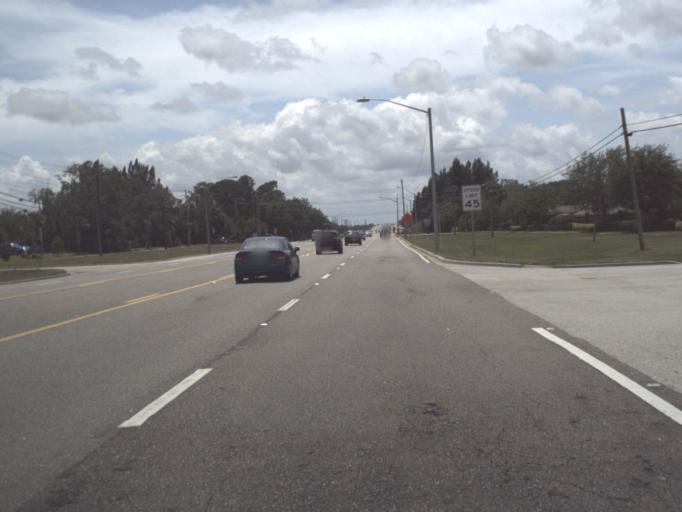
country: US
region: Florida
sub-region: Brevard County
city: Rockledge
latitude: 28.3047
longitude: -80.7429
